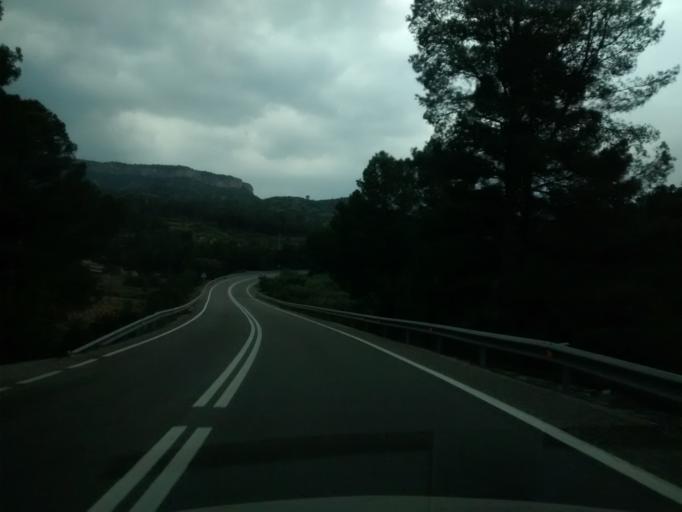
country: ES
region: Catalonia
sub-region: Provincia de Tarragona
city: Benifallet
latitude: 41.0215
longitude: 0.4999
